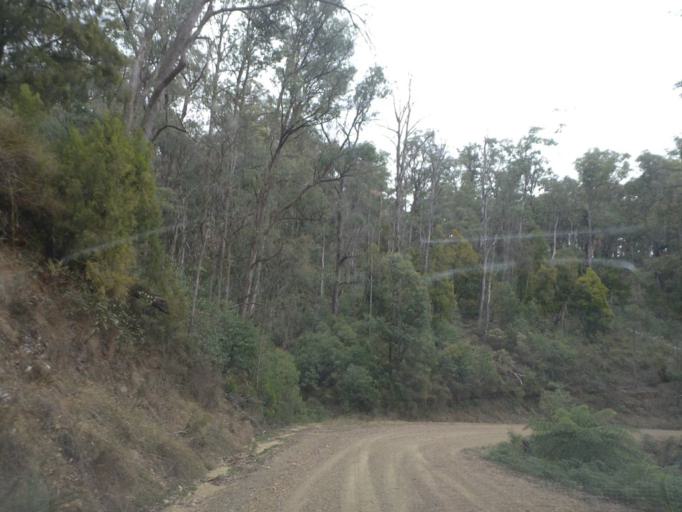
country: AU
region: Victoria
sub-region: Murrindindi
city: Alexandra
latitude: -37.4462
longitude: 145.9652
